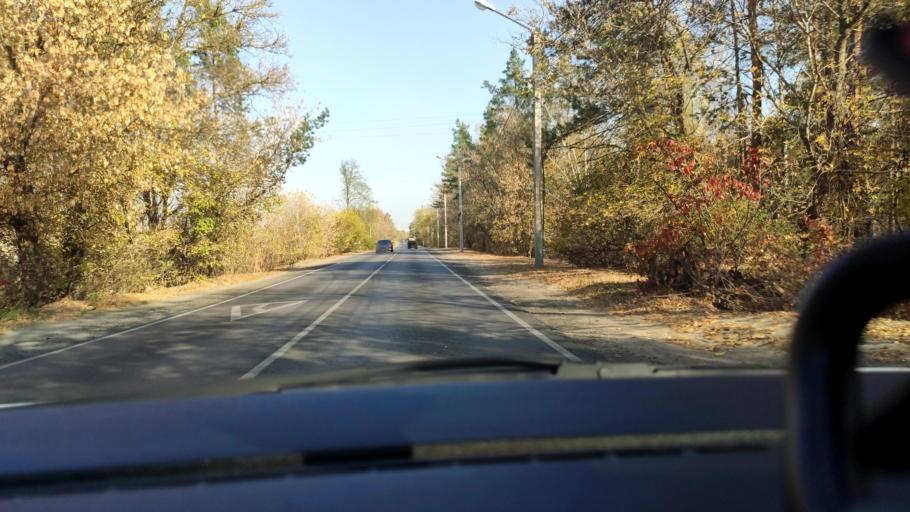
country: RU
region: Voronezj
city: Pridonskoy
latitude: 51.6341
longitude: 39.0833
